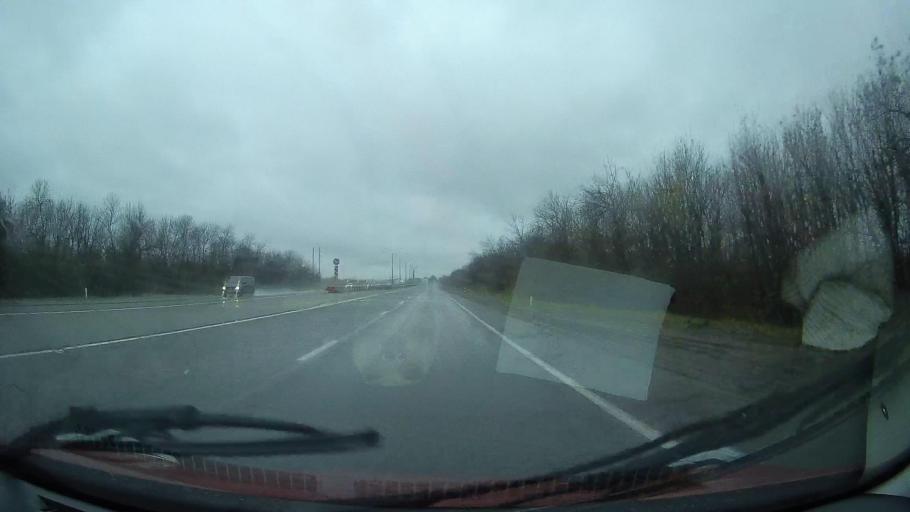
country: RU
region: Stavropol'skiy
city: Nevinnomyssk
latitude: 44.6352
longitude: 42.0018
